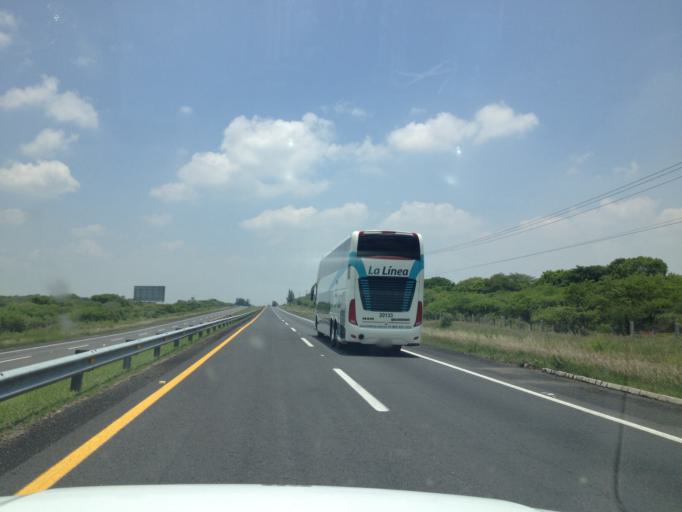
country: MX
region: Michoacan
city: Churintzio
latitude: 20.1389
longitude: -102.0785
